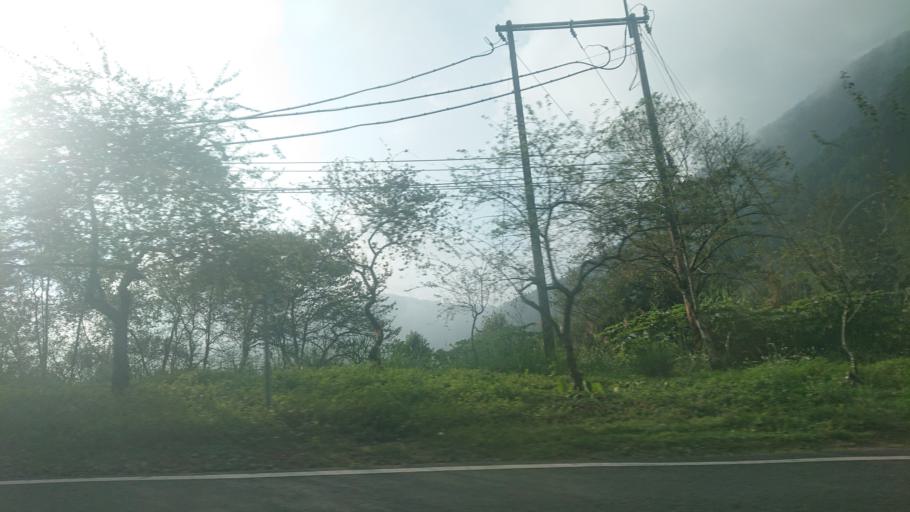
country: TW
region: Taiwan
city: Lugu
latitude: 23.4954
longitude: 120.7927
